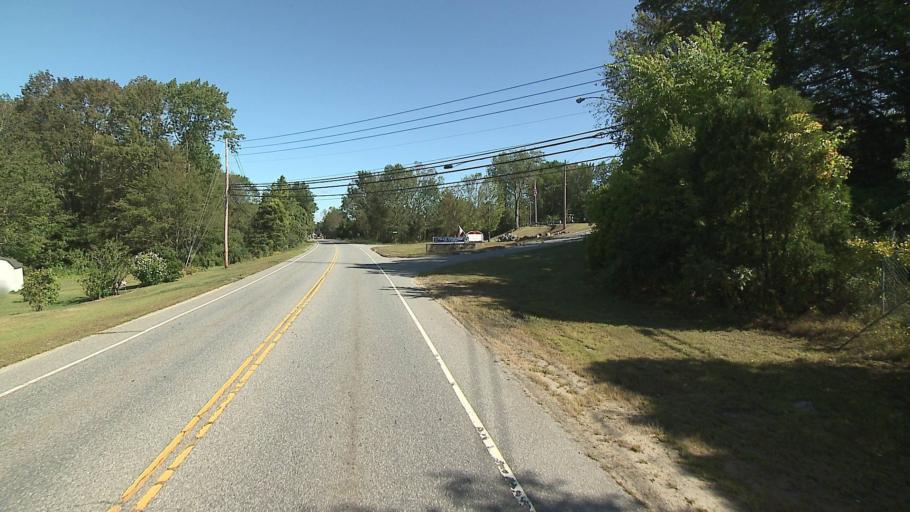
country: US
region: Connecticut
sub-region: Windham County
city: Moosup
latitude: 41.7046
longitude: -71.9055
